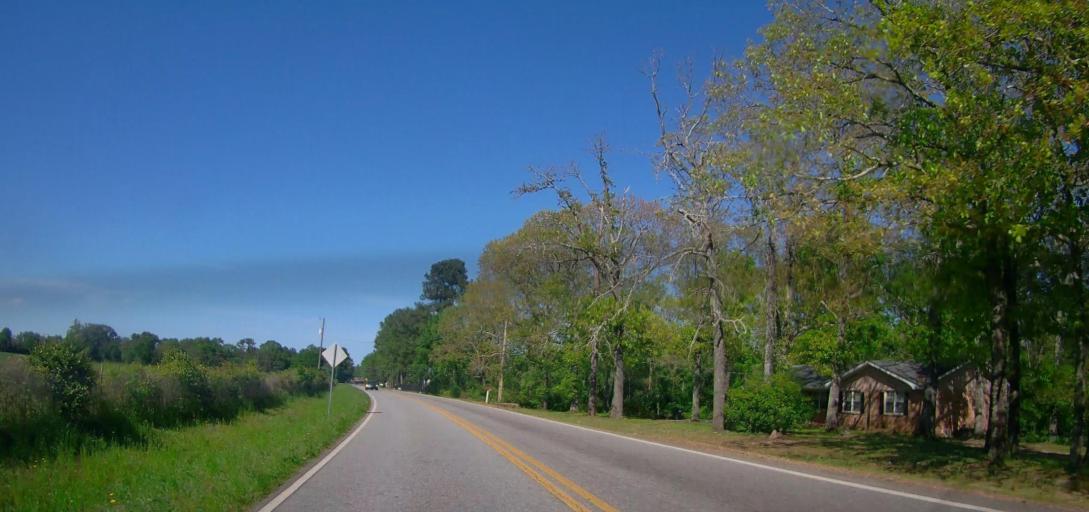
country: US
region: Georgia
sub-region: Houston County
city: Warner Robins
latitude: 32.6519
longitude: -83.6398
